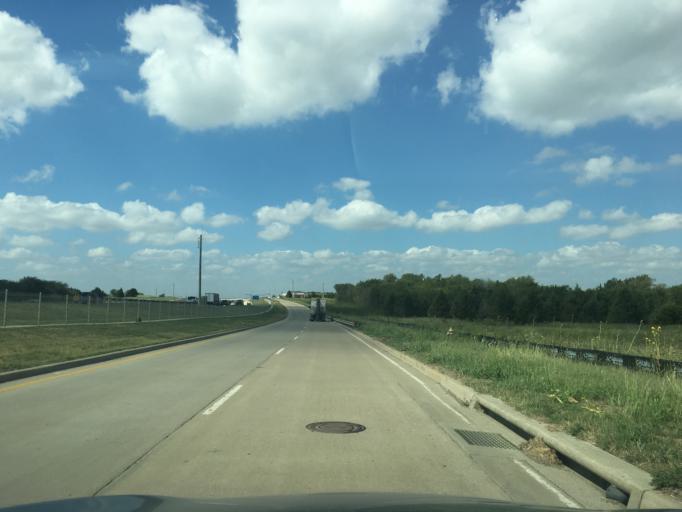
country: US
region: Texas
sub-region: Dallas County
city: Sachse
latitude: 32.9519
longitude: -96.5770
